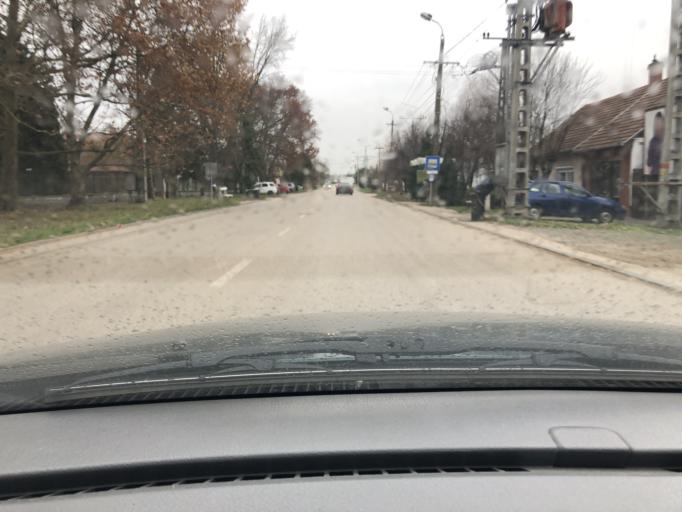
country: HU
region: Csongrad
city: Csongrad
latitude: 46.7031
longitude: 20.1471
